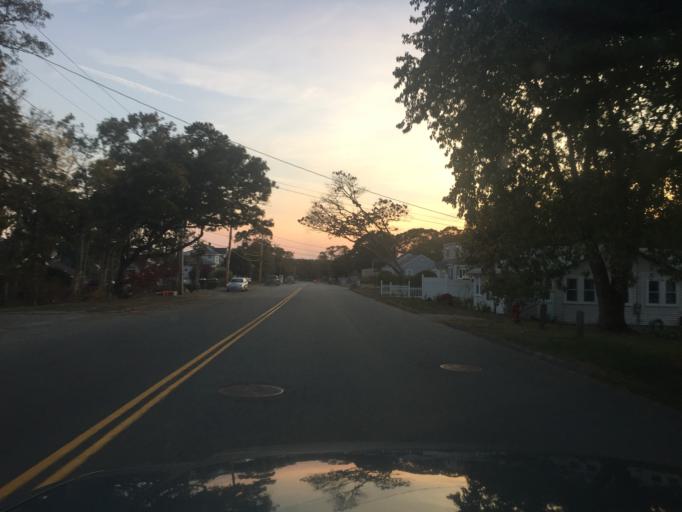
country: US
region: Massachusetts
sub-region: Plymouth County
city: Onset
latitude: 41.7513
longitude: -70.6538
